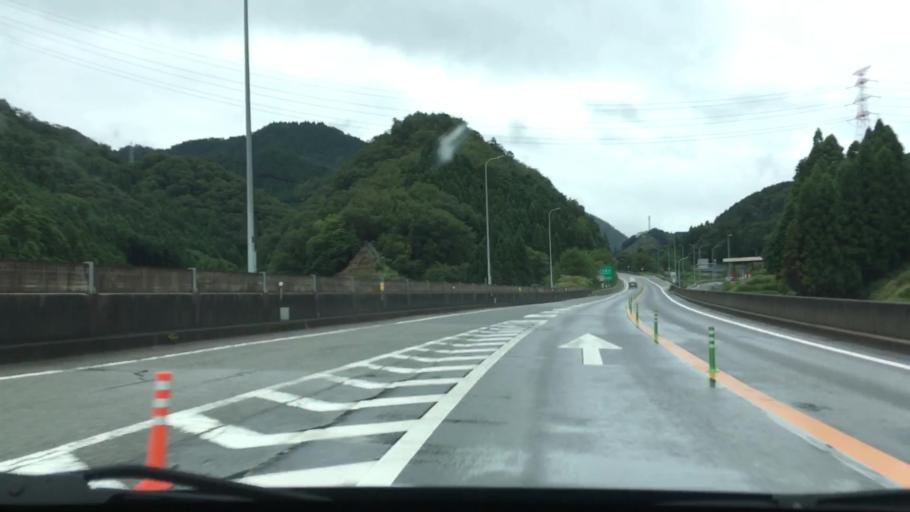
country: JP
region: Hyogo
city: Nishiwaki
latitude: 35.1871
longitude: 134.7920
